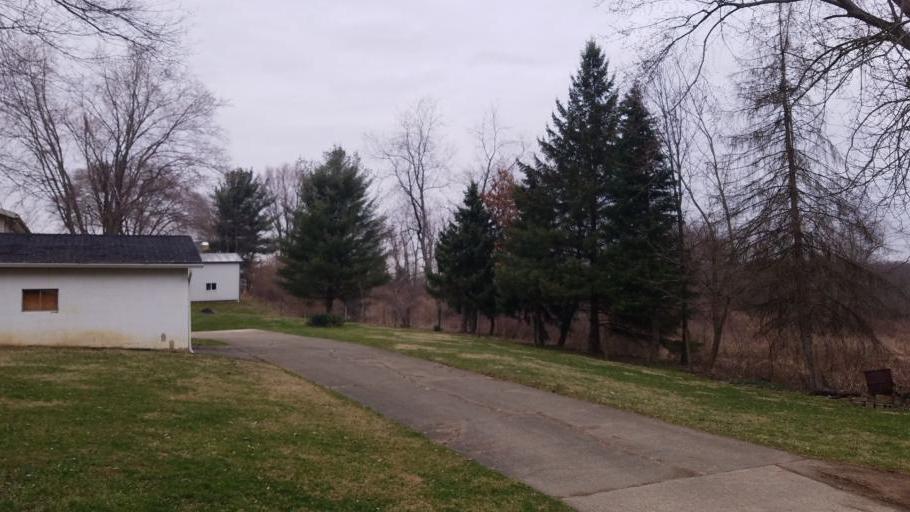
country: US
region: Ohio
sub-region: Knox County
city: Fredericktown
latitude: 40.5028
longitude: -82.5121
